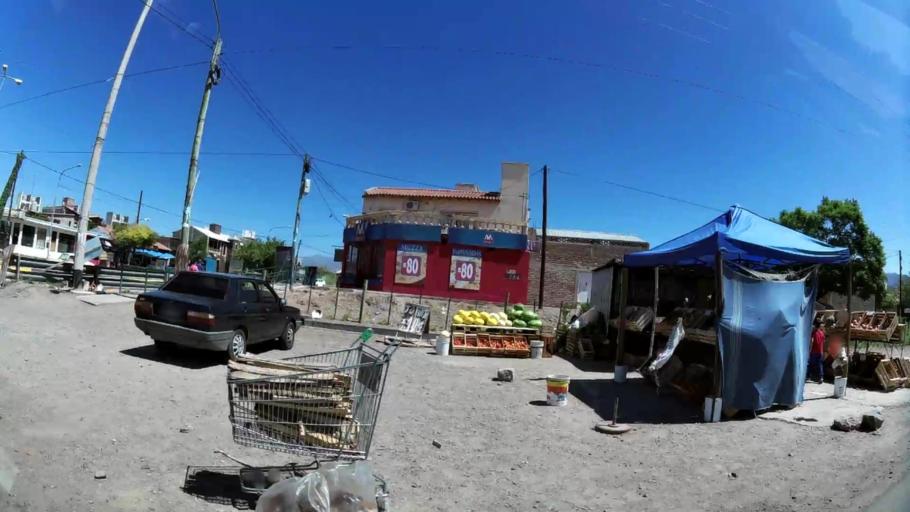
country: AR
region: Mendoza
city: Las Heras
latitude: -32.8463
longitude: -68.8609
